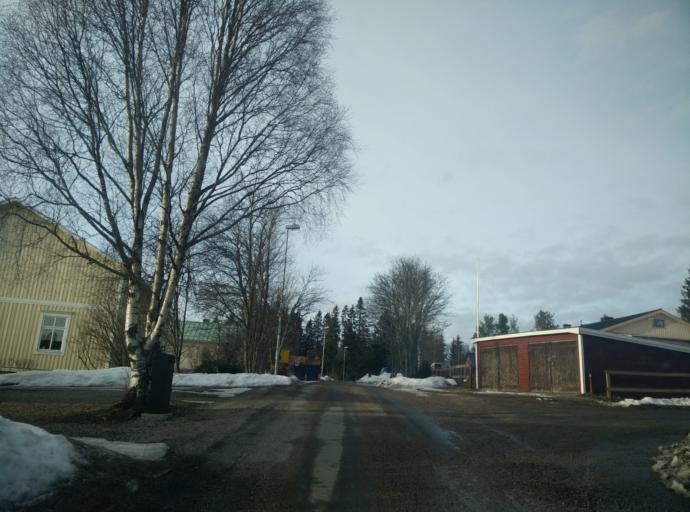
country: SE
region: Vaesternorrland
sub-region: Sundsvalls Kommun
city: Johannedal
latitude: 62.4345
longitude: 17.4196
